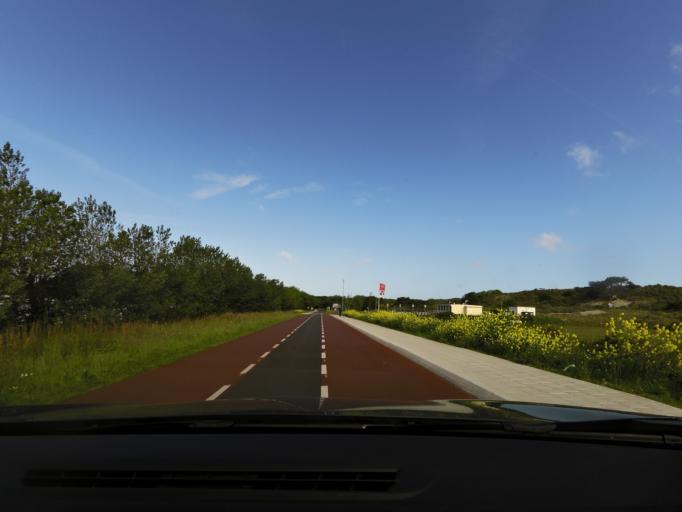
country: NL
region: Zeeland
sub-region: Schouwen-Duiveland
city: Renesse
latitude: 51.7411
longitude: 3.7922
